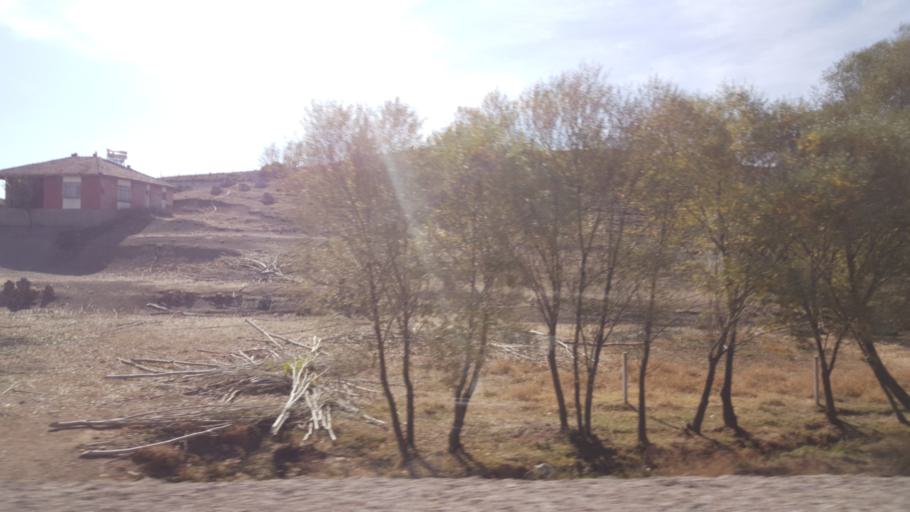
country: TR
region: Ankara
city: Haymana
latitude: 39.4205
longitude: 32.5928
